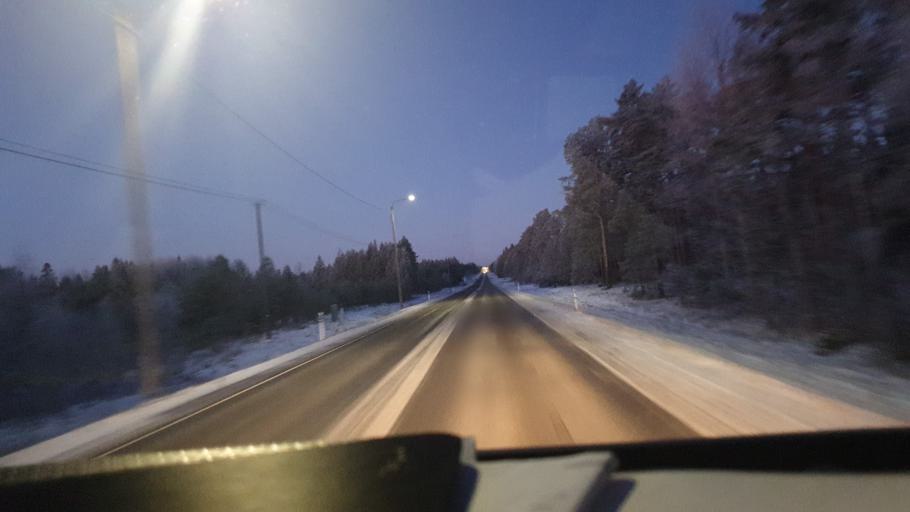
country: FI
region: Northern Ostrobothnia
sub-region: Raahe
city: Siikajoki
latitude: 64.6948
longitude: 24.6898
